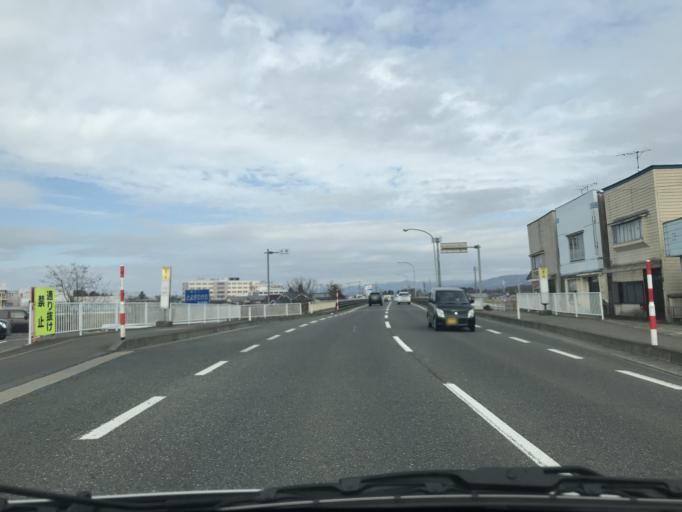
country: JP
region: Iwate
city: Hanamaki
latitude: 39.3805
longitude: 141.1207
